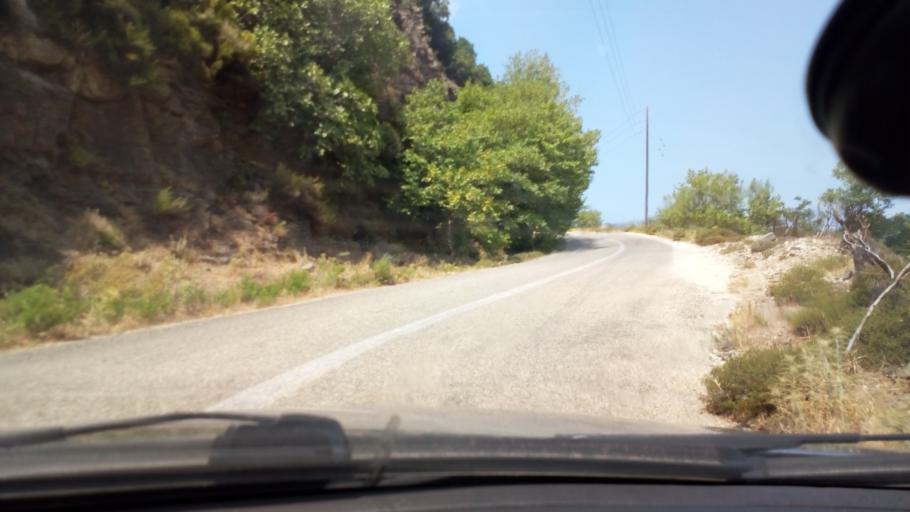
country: GR
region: North Aegean
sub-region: Nomos Samou
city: Agios Kirykos
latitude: 37.6357
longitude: 26.2585
